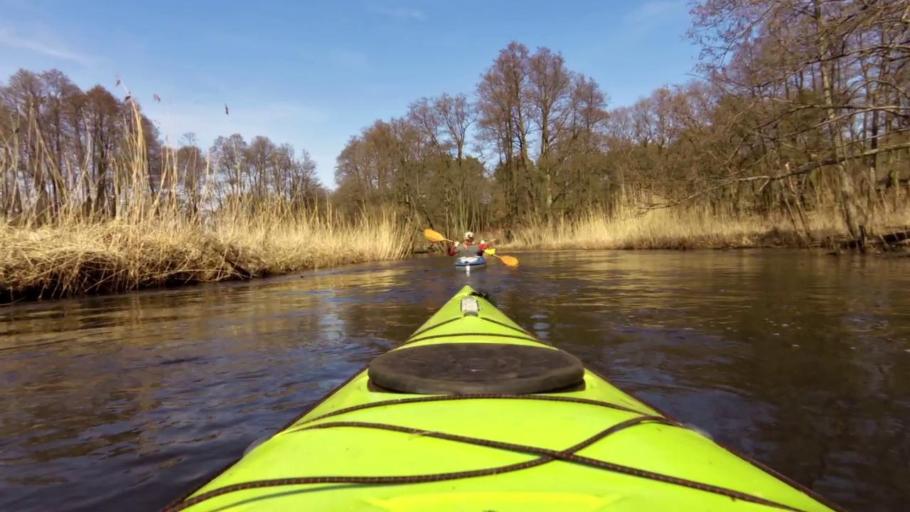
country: PL
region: West Pomeranian Voivodeship
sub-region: Powiat lobeski
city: Lobez
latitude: 53.6706
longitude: 15.5661
